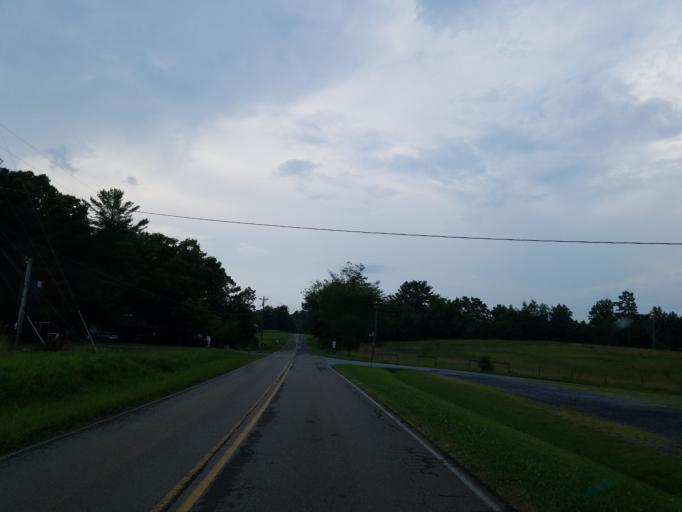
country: US
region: Georgia
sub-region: Pickens County
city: Jasper
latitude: 34.4841
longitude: -84.5107
